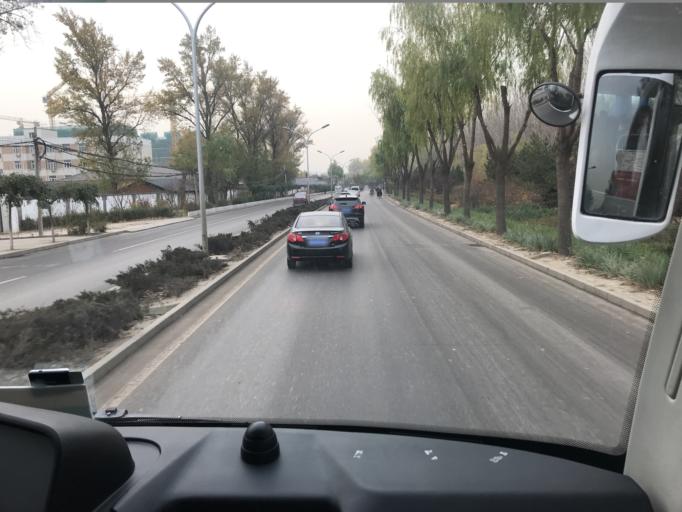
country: CN
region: Beijing
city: Sujiatuo
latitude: 40.0967
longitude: 116.2081
